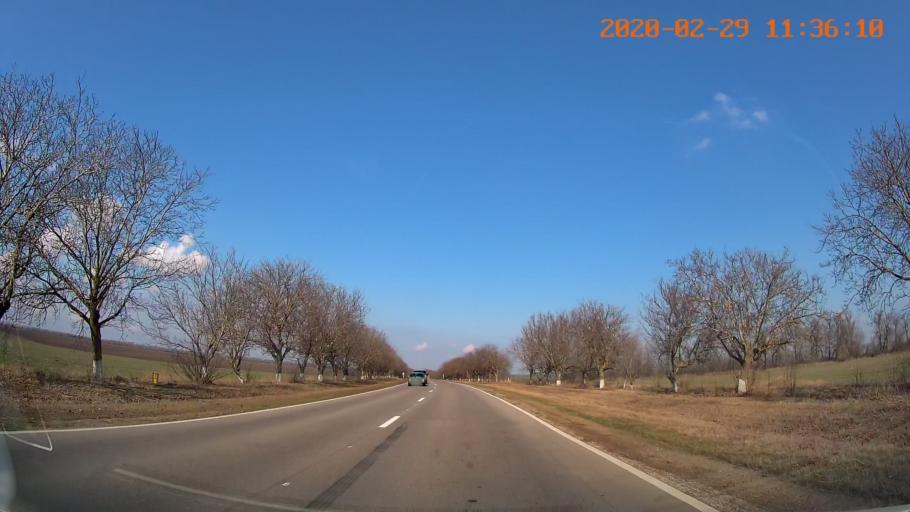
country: MD
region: Rezina
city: Saharna
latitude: 47.5920
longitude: 29.0583
